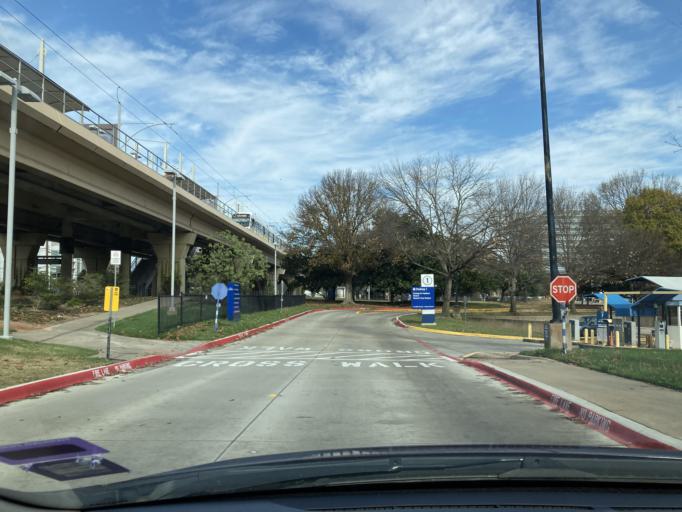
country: US
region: Texas
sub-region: Dallas County
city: University Park
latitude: 32.8818
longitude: -96.7647
